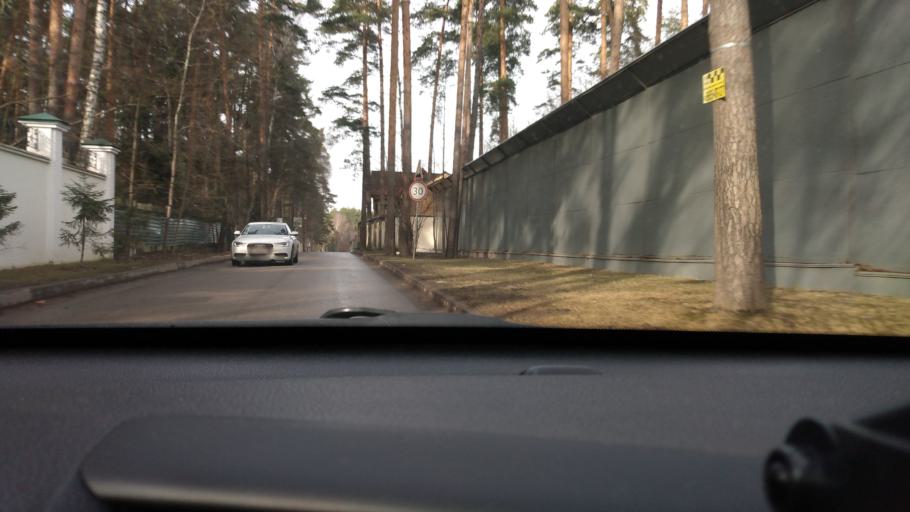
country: RU
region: Moskovskaya
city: Barvikha
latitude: 55.7309
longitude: 37.2483
